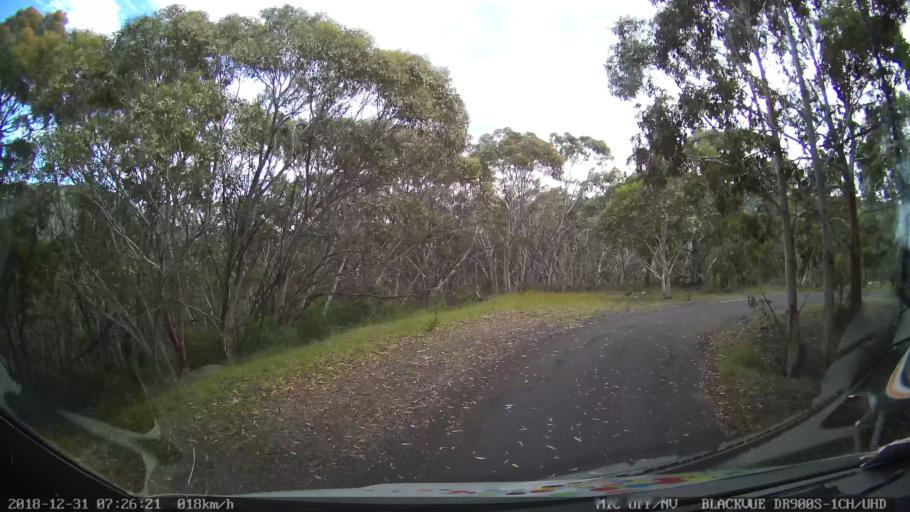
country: AU
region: New South Wales
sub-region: Snowy River
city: Jindabyne
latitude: -36.3183
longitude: 148.4806
